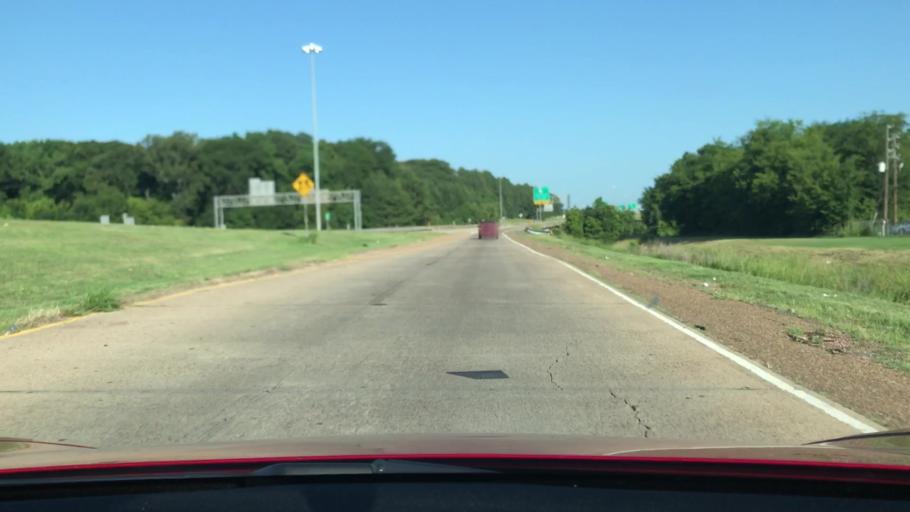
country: US
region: Louisiana
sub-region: Bossier Parish
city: Bossier City
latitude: 32.4125
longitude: -93.7262
